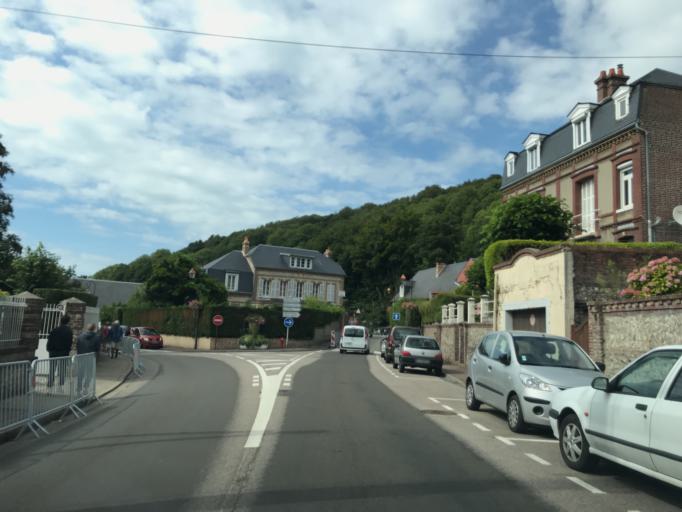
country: FR
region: Haute-Normandie
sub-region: Departement de la Seine-Maritime
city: Yport
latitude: 49.7361
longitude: 0.3176
